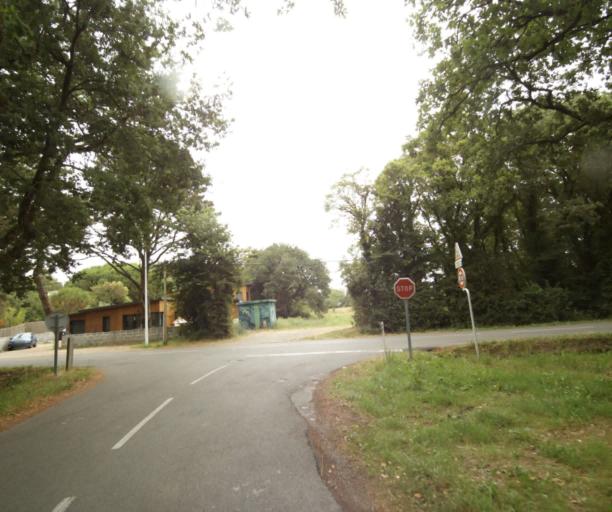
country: FR
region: Pays de la Loire
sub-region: Departement de la Vendee
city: Chateau-d'Olonne
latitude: 46.4820
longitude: -1.7271
